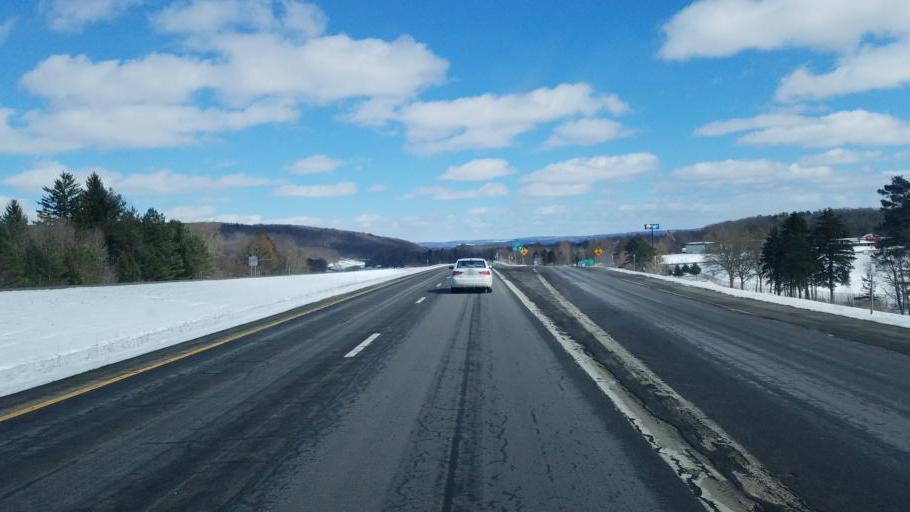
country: US
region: New York
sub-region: Chautauqua County
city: Jamestown
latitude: 42.1207
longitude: -79.2452
